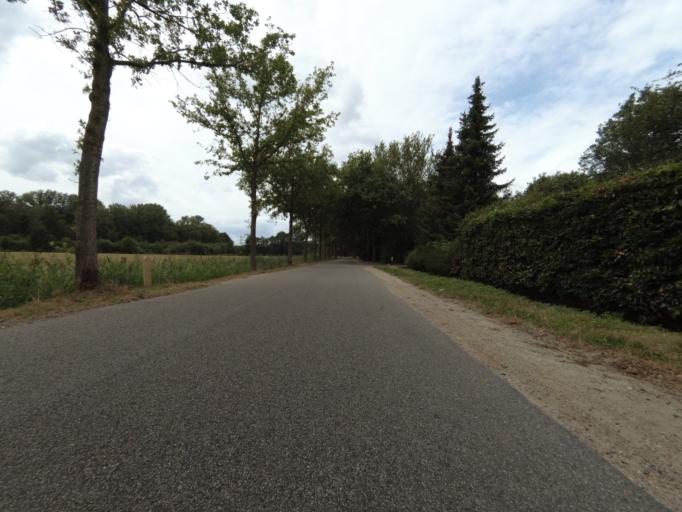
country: NL
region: Overijssel
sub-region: Gemeente Enschede
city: Enschede
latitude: 52.2031
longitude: 6.9385
